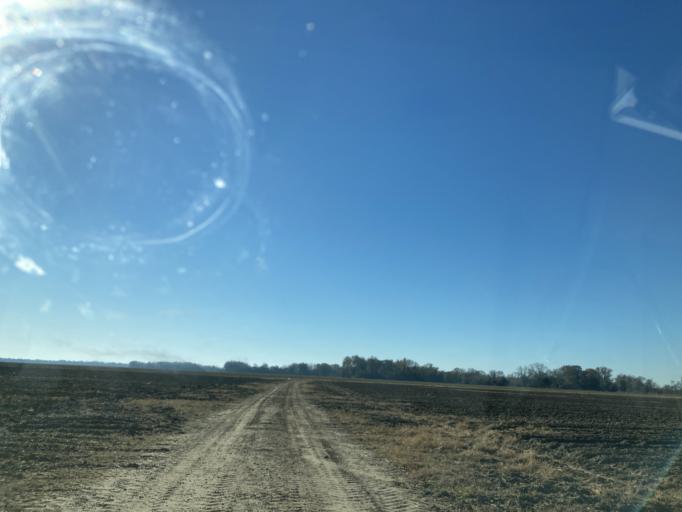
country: US
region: Mississippi
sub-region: Sharkey County
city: Rolling Fork
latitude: 32.8592
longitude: -90.6938
